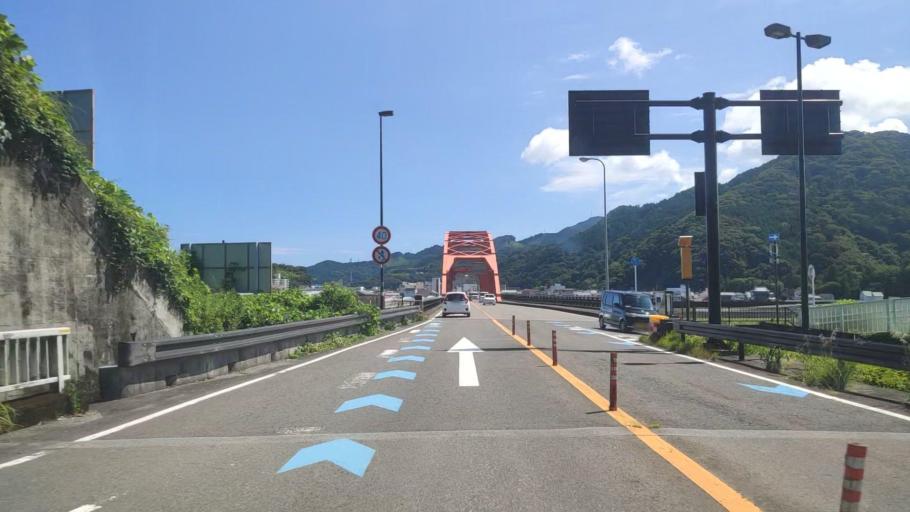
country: JP
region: Wakayama
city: Shingu
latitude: 33.7352
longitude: 135.9882
